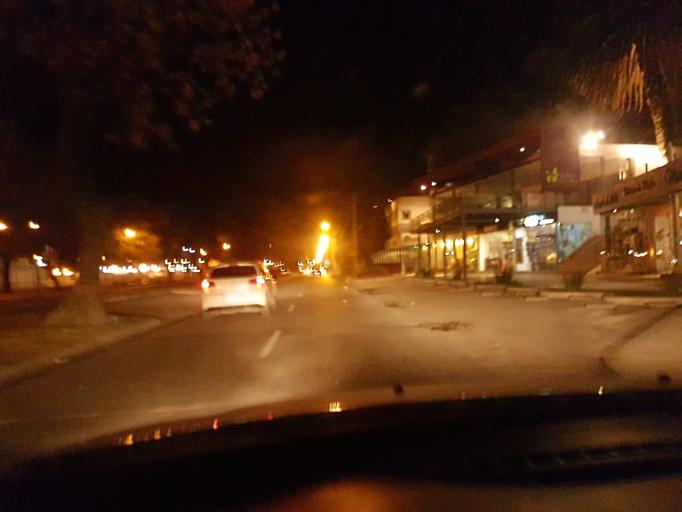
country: AR
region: Cordoba
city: Villa Allende
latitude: -31.2907
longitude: -64.2920
